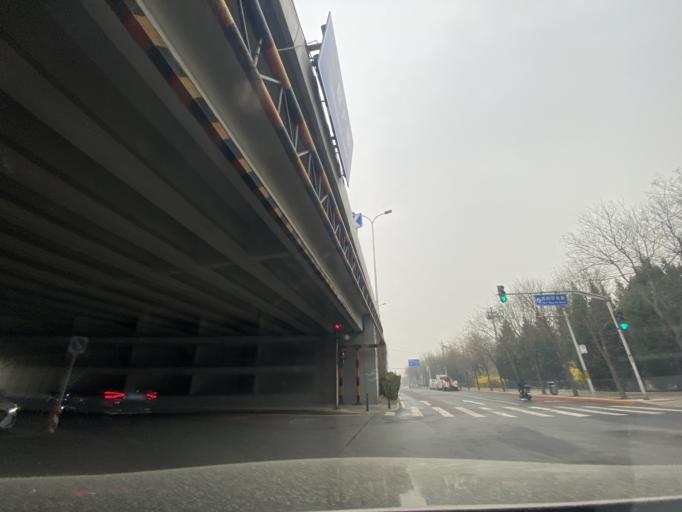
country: CN
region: Beijing
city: Sijiqing
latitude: 39.9654
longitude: 116.2682
